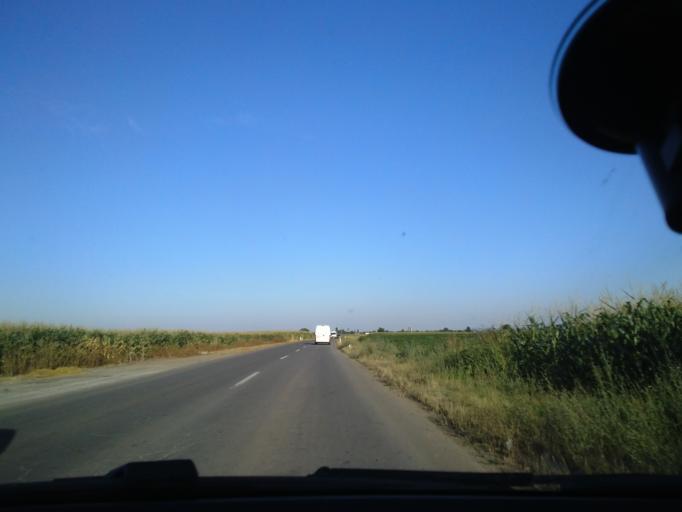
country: RS
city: Maglic
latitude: 45.4039
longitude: 19.4325
